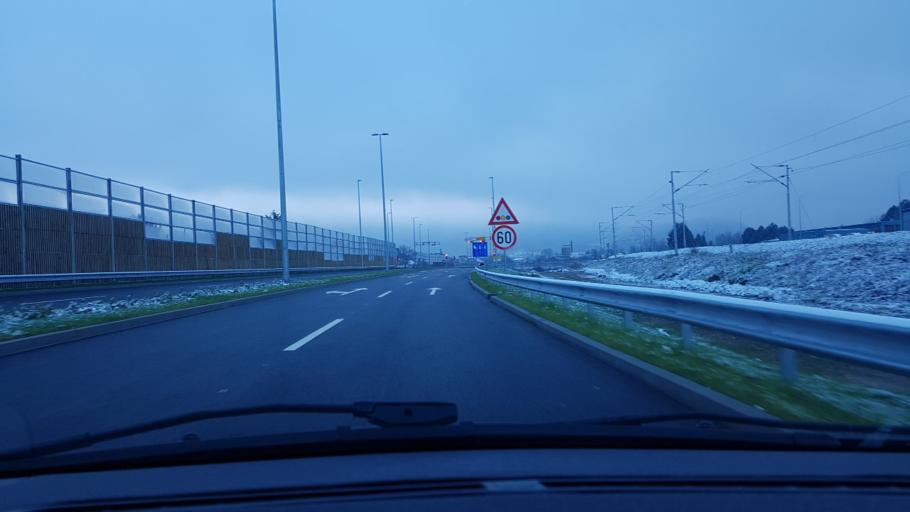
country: HR
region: Zagrebacka
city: Zapresic
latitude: 45.8522
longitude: 15.8046
